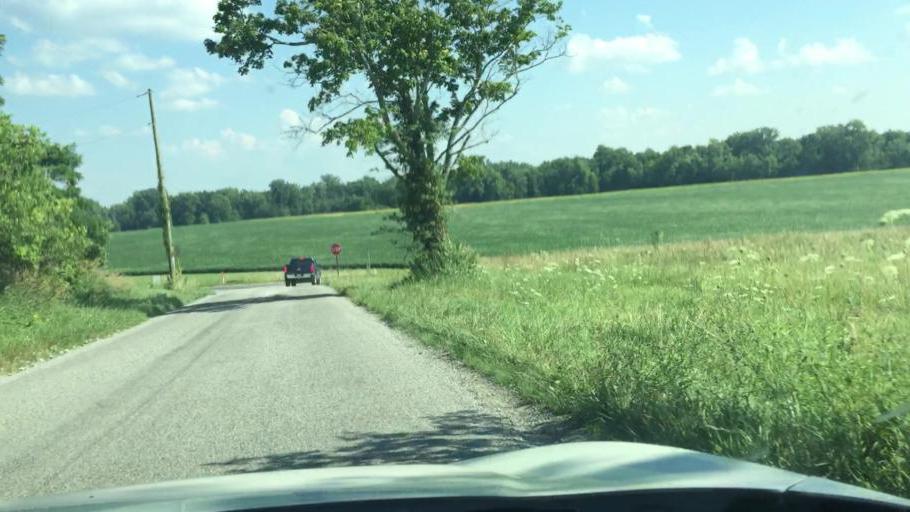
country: US
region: Ohio
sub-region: Champaign County
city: North Lewisburg
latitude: 40.2301
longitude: -83.5149
